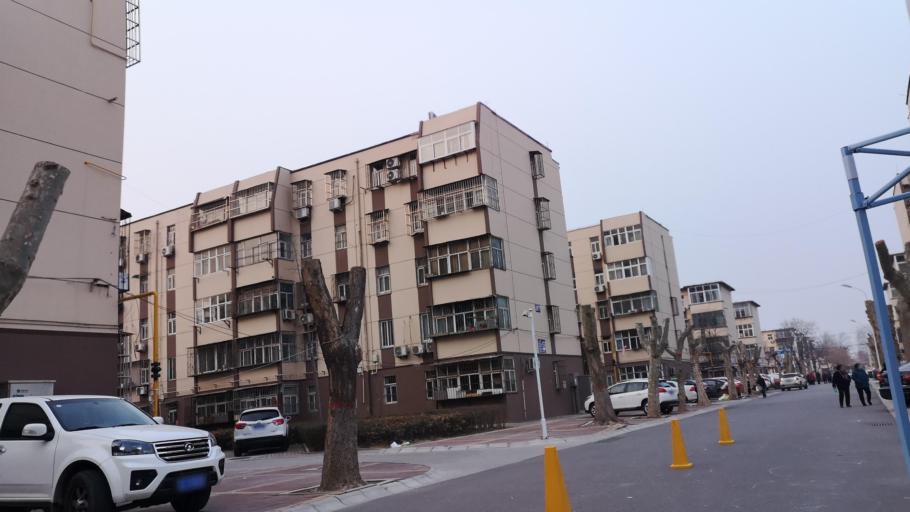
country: CN
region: Henan Sheng
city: Zhongyuanlu
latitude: 35.7833
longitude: 115.0731
